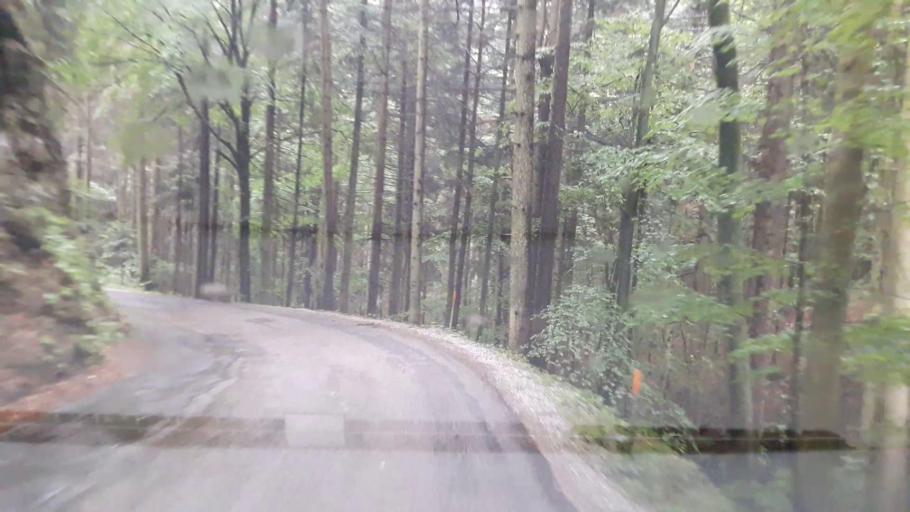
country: AT
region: Lower Austria
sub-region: Politischer Bezirk Krems
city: Aggsbach
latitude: 48.2921
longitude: 15.3685
